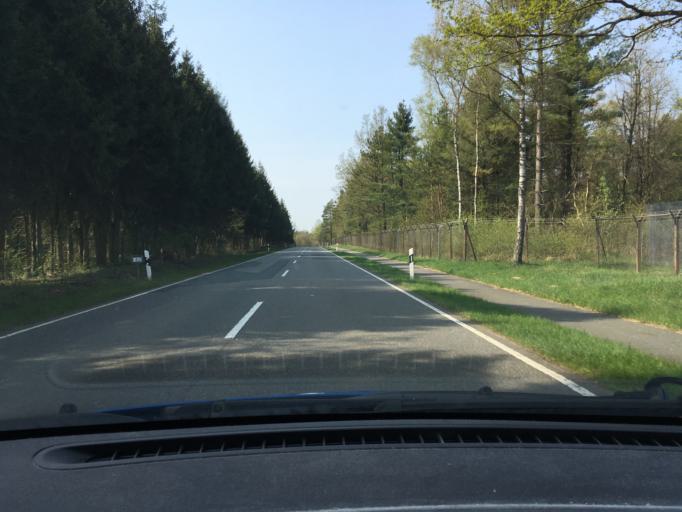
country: DE
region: Lower Saxony
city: Unterluss
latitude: 52.8588
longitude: 10.2744
